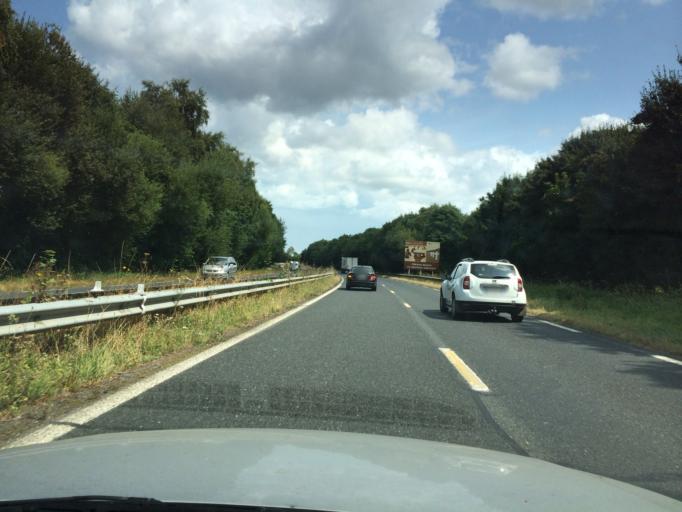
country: FR
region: Lower Normandy
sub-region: Departement du Calvados
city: Grandcamp-Maisy
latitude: 49.3413
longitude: -0.9765
